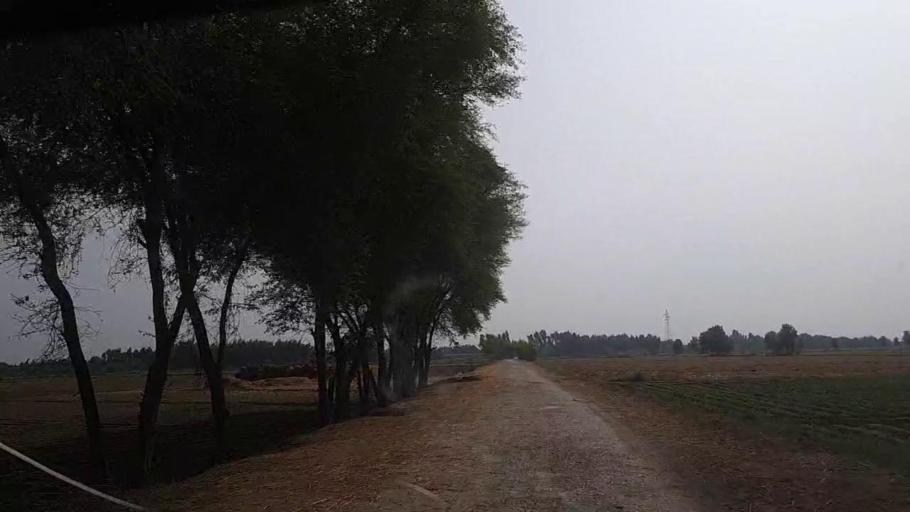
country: PK
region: Sindh
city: Madeji
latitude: 27.7379
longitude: 68.4357
